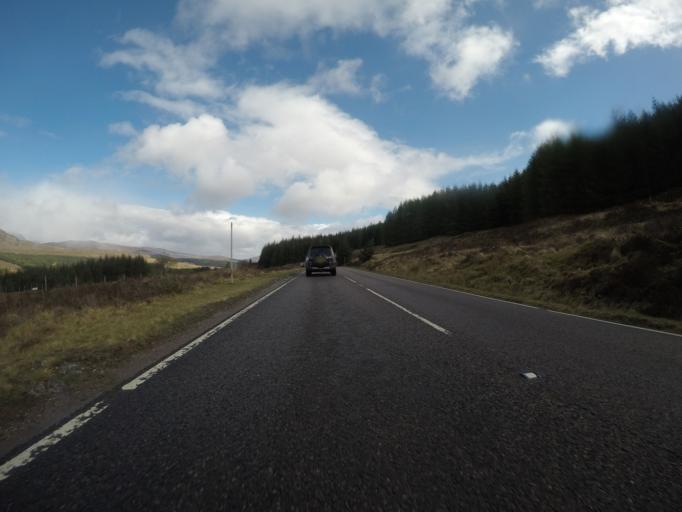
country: GB
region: Scotland
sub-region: Highland
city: Spean Bridge
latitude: 57.1061
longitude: -4.9855
